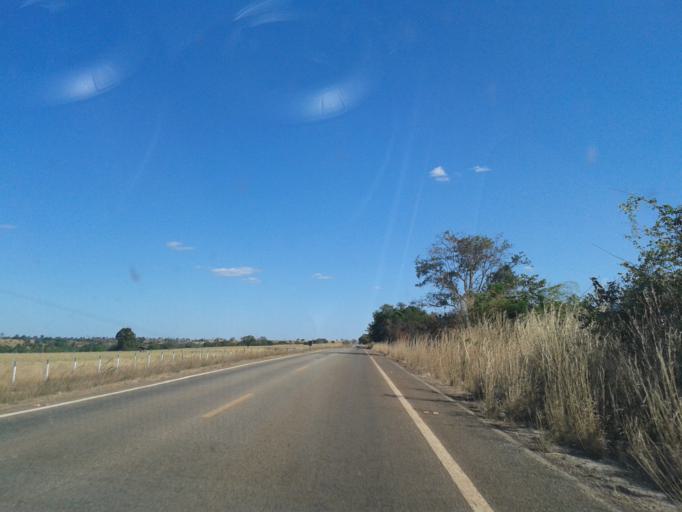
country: BR
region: Goias
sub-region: Mozarlandia
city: Mozarlandia
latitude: -14.3662
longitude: -50.4287
